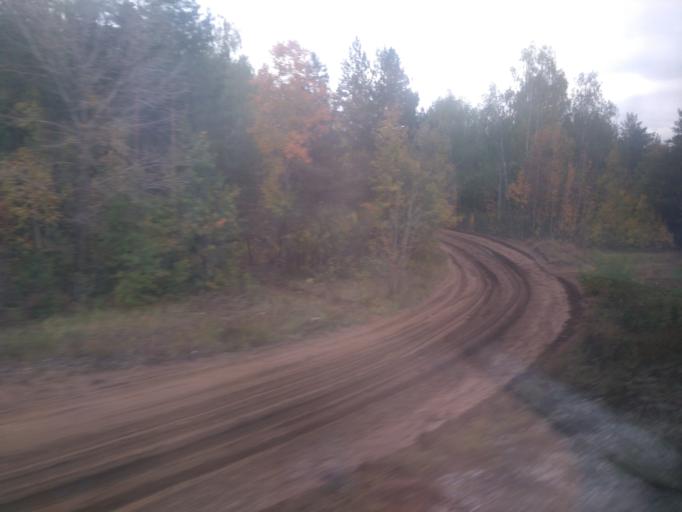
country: RU
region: Tatarstan
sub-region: Tukayevskiy Rayon
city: Naberezhnyye Chelny
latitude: 55.7247
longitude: 52.2585
